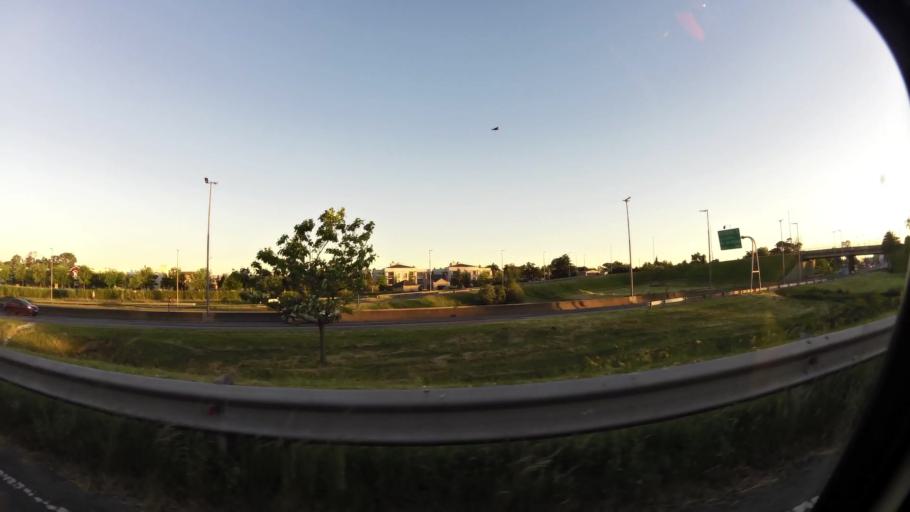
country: AR
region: Buenos Aires
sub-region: Partido de Quilmes
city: Quilmes
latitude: -34.8208
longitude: -58.1889
